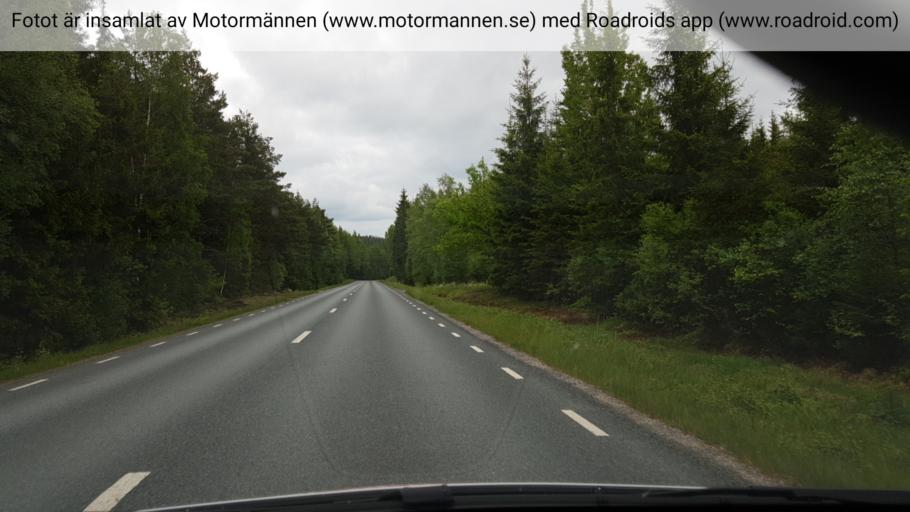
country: SE
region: Joenkoeping
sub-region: Vetlanda Kommun
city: Vetlanda
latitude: 57.3951
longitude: 15.1713
